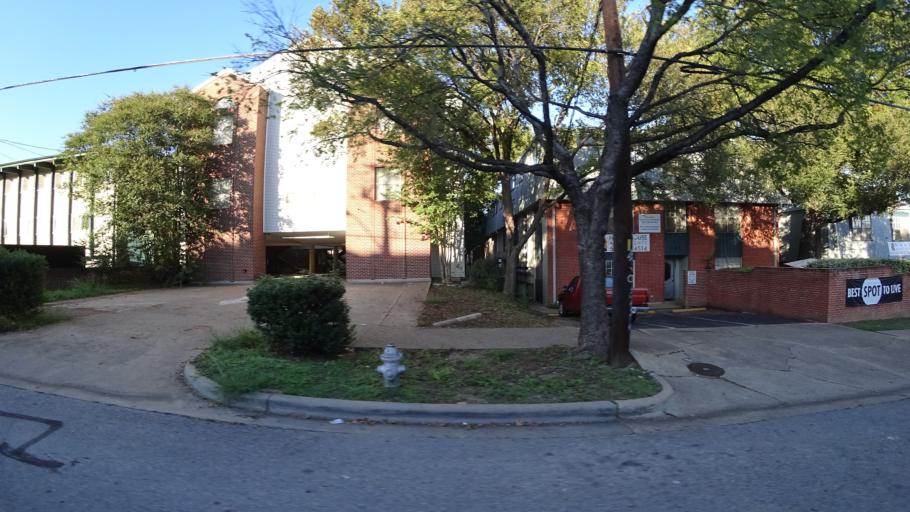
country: US
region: Texas
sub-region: Travis County
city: Austin
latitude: 30.2924
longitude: -97.7350
